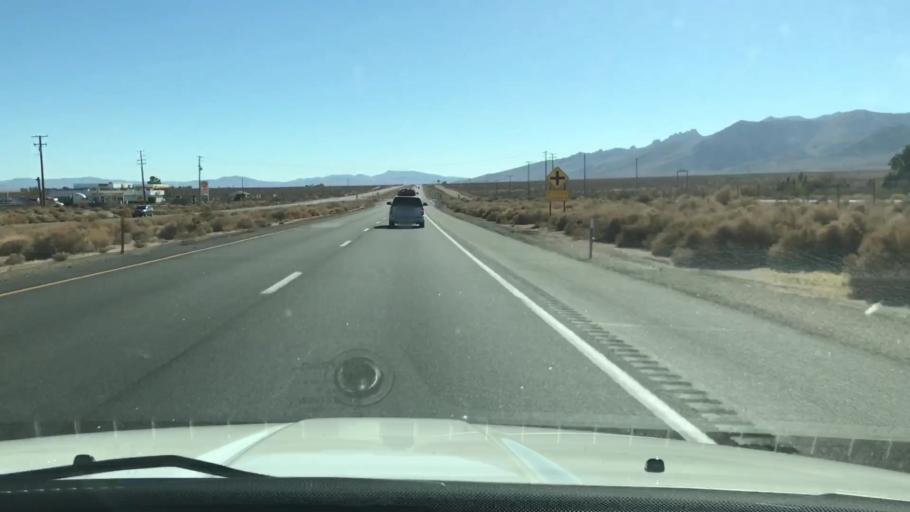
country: US
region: California
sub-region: Kern County
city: Inyokern
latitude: 35.8012
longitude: -117.8752
